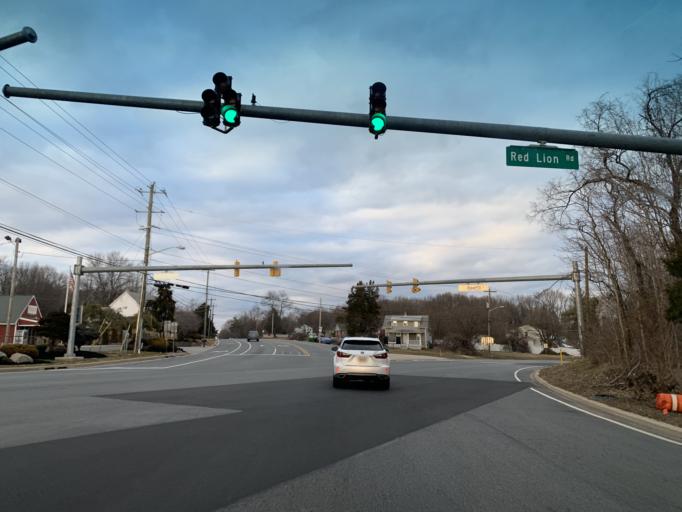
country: US
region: Delaware
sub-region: New Castle County
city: Bear
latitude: 39.6082
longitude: -75.6644
